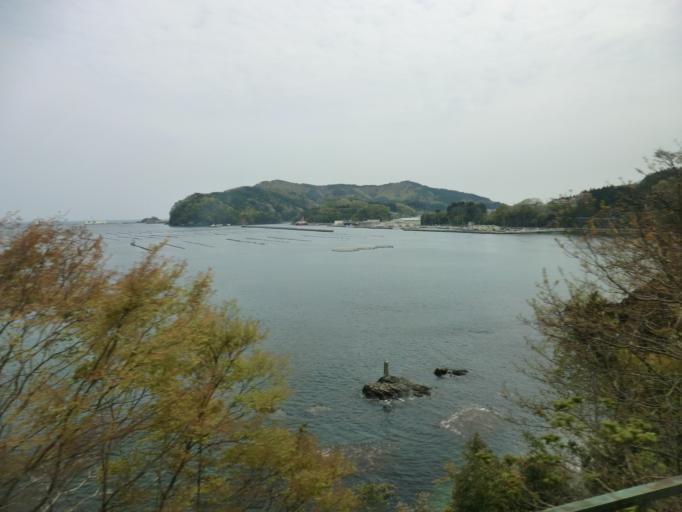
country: JP
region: Iwate
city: Ofunato
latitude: 39.0316
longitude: 141.7155
